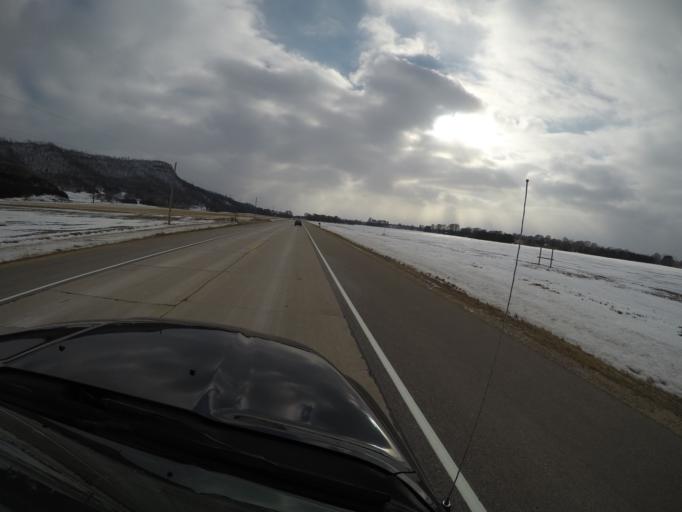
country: US
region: Wisconsin
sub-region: La Crosse County
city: Holmen
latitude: 44.0195
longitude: -91.2888
